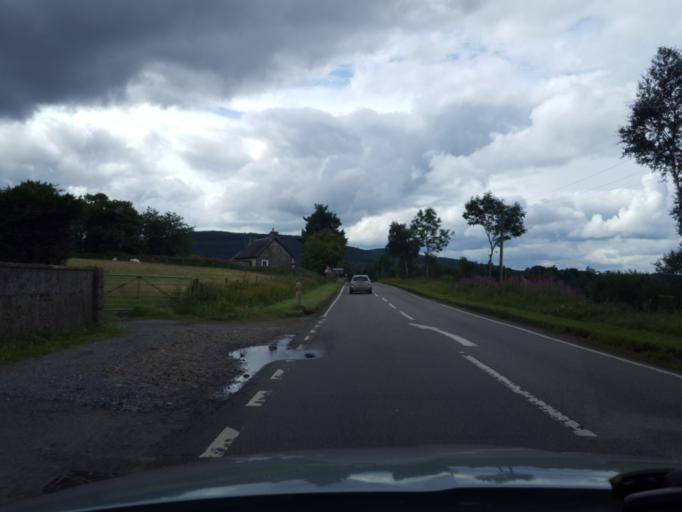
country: GB
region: Scotland
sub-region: Moray
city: Rothes
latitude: 57.4221
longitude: -3.3545
